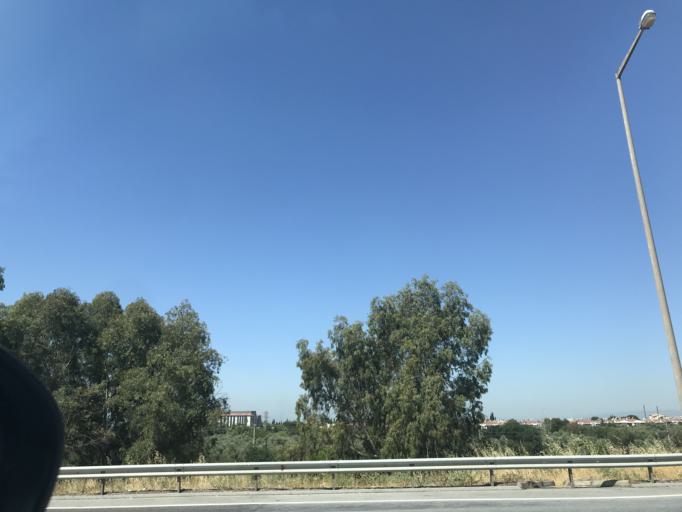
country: TR
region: Aydin
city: Aydin
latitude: 37.8495
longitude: 27.8070
